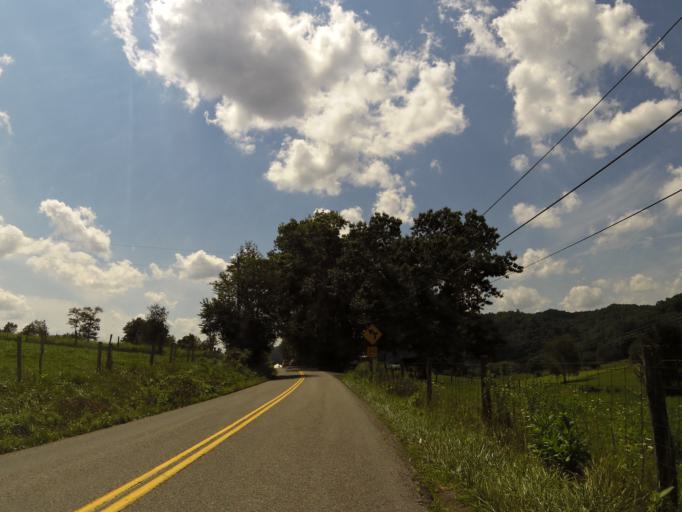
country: US
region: Virginia
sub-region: Washington County
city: Abingdon
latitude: 36.6698
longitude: -81.9608
